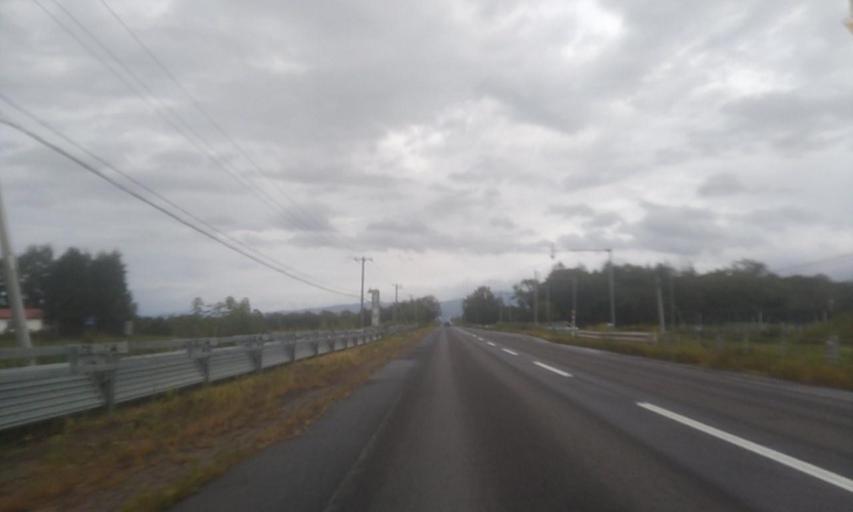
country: JP
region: Hokkaido
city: Abashiri
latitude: 43.8993
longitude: 144.6307
